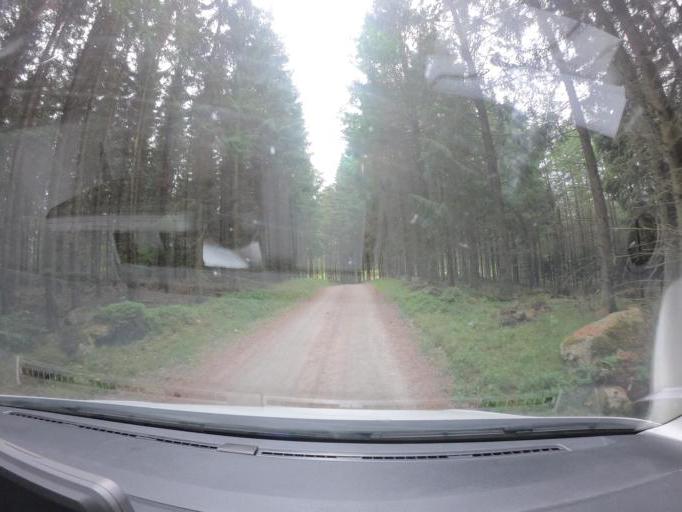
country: SE
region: Skane
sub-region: Hassleholms Kommun
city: Sosdala
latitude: 56.0168
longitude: 13.6107
